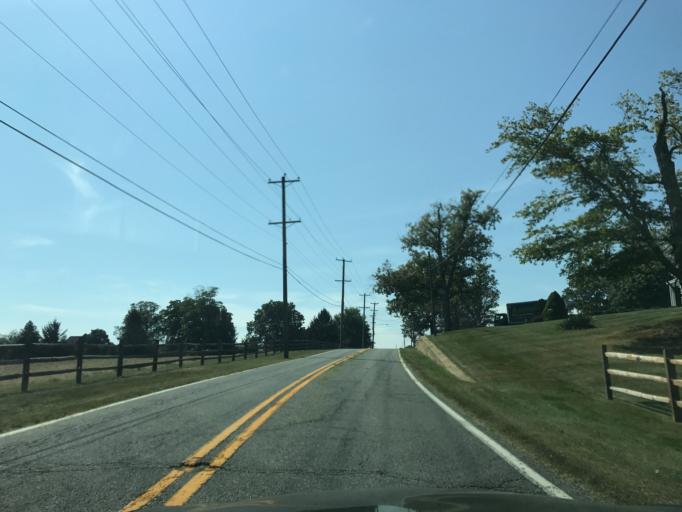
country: US
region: Maryland
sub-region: Cecil County
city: Perryville
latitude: 39.5772
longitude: -76.0332
